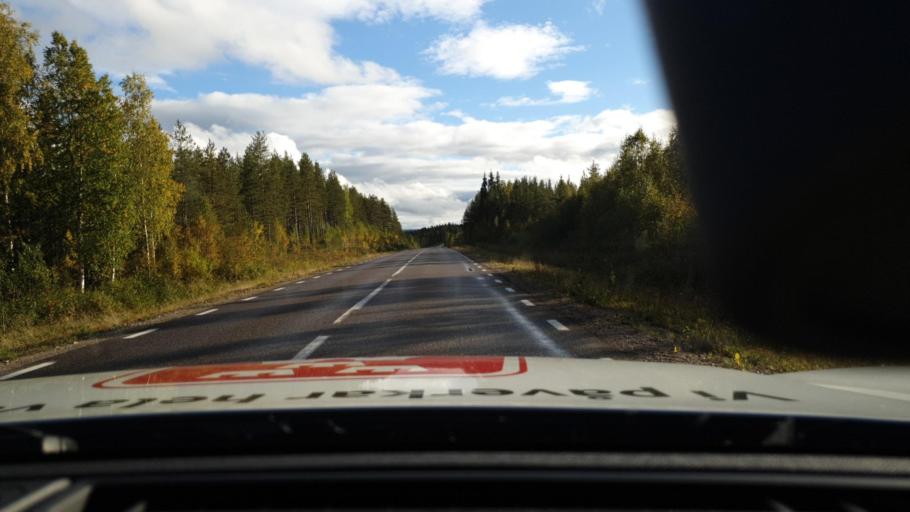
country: SE
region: Norrbotten
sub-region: Overkalix Kommun
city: OEverkalix
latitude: 66.7411
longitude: 22.6703
